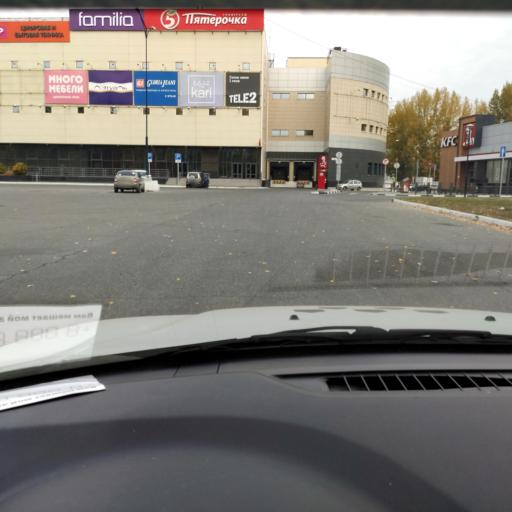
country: RU
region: Samara
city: Tol'yatti
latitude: 53.5100
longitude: 49.4584
